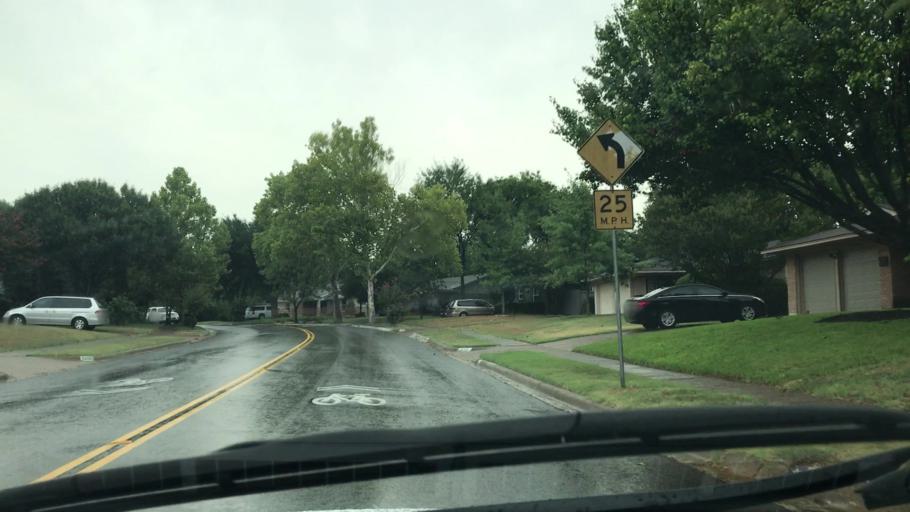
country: US
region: Texas
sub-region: Dallas County
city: Richardson
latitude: 32.9292
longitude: -96.7744
